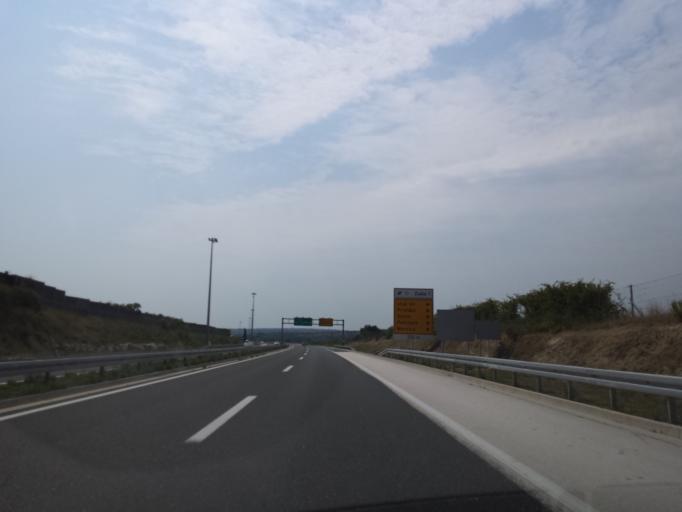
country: HR
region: Zadarska
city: Posedarje
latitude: 44.1911
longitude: 15.4357
